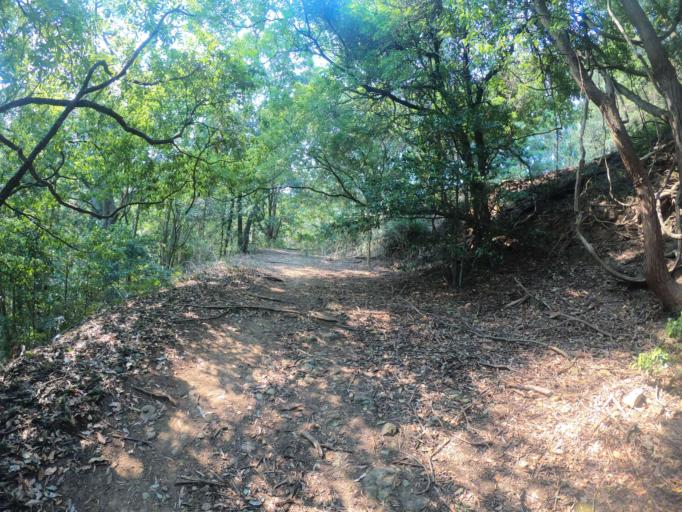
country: AU
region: New South Wales
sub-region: Wollongong
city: Bulli
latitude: -34.3240
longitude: 150.8884
